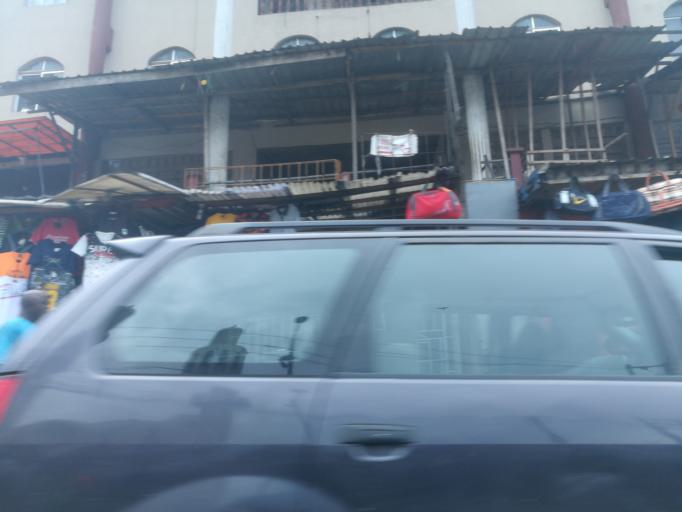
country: NG
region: Lagos
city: Lagos
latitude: 6.4575
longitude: 3.3877
